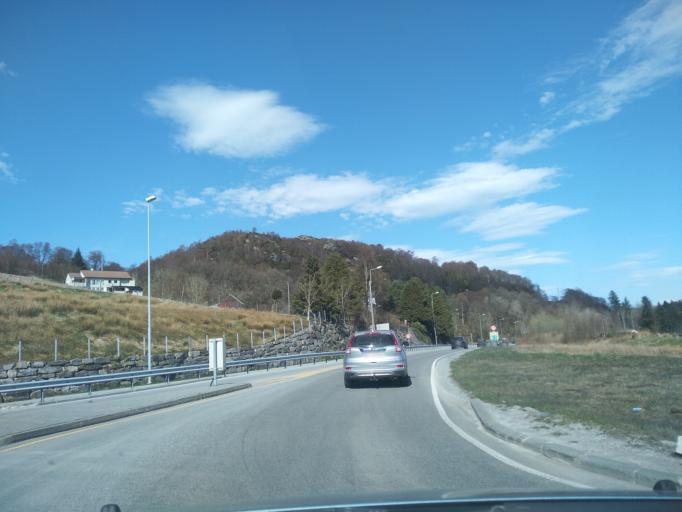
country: NO
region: Rogaland
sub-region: Tysvaer
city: Aksdal
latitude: 59.4261
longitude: 5.4594
